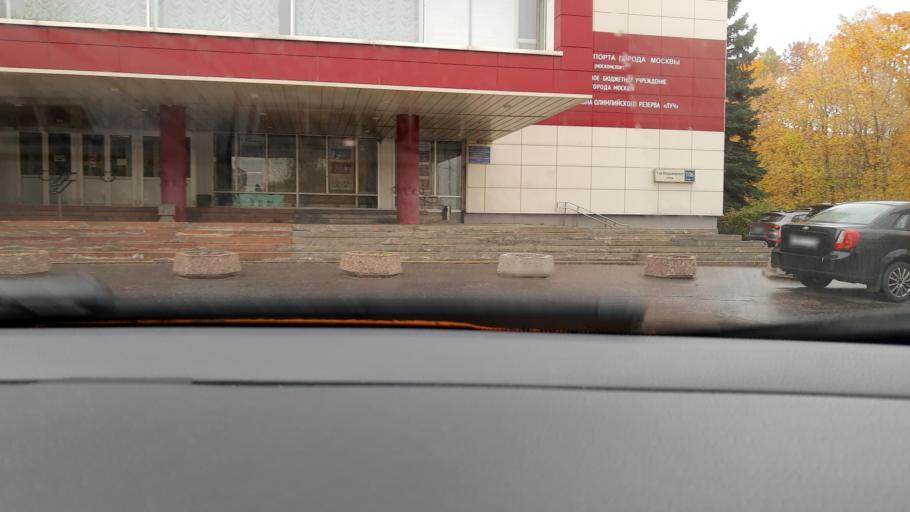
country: RU
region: Moscow
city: Ryazanskiy
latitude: 55.7585
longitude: 37.7720
